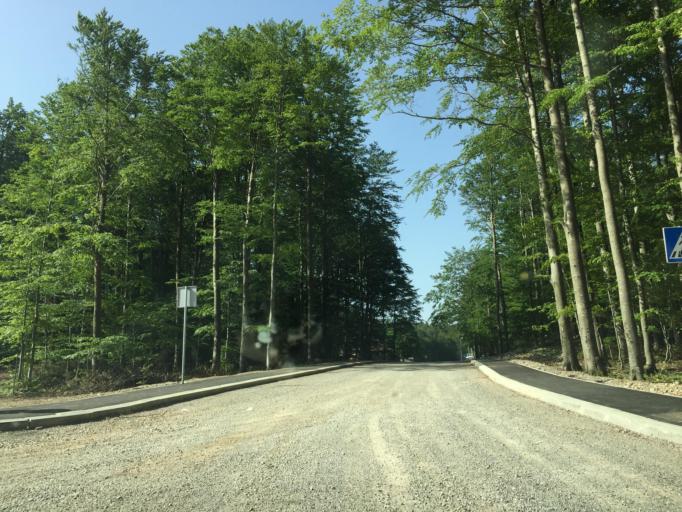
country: HR
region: Primorsko-Goranska
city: Podhum
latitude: 45.4272
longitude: 14.5665
